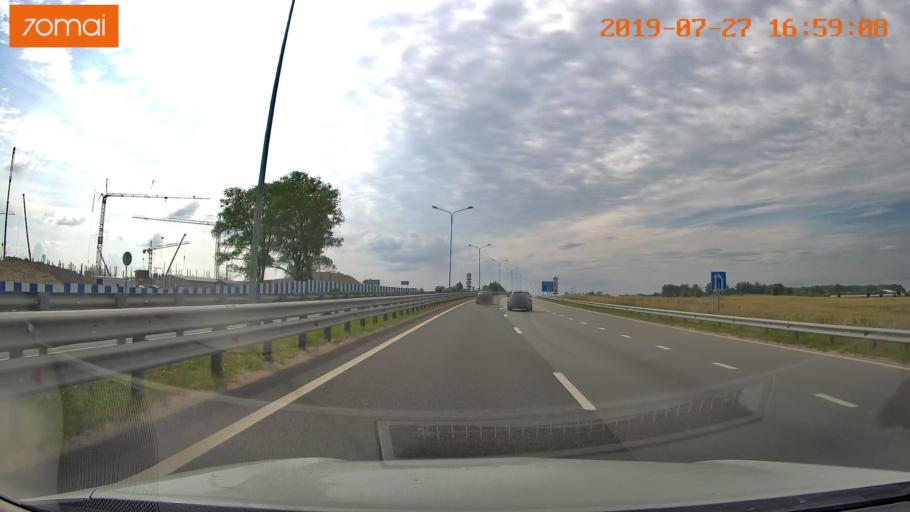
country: RU
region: Kaliningrad
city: Bol'shoe Isakovo
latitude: 54.7024
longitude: 20.6590
